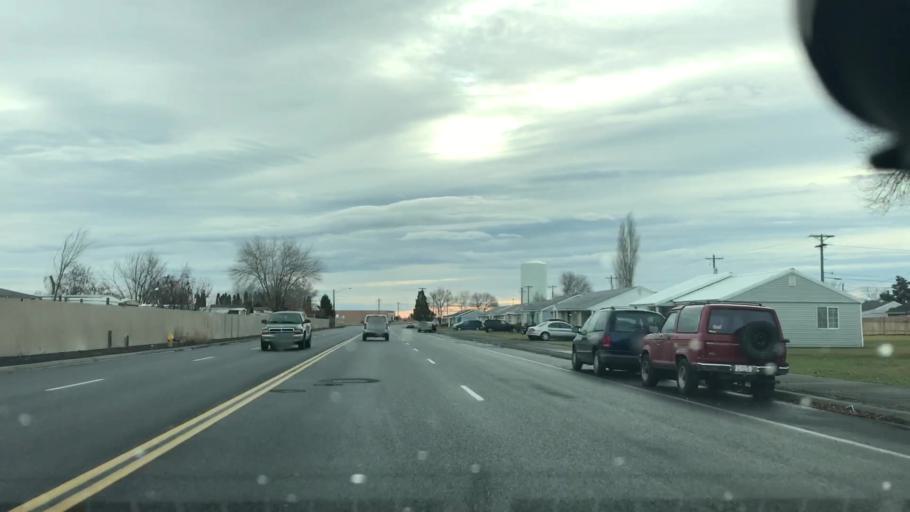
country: US
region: Washington
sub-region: Grant County
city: Moses Lake North
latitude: 47.1766
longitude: -119.3212
